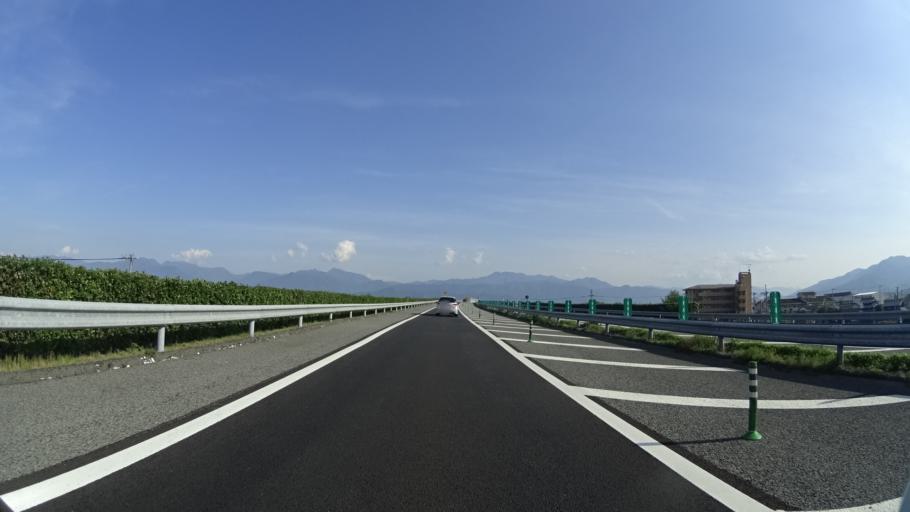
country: JP
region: Ehime
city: Saijo
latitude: 33.9540
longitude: 133.0685
